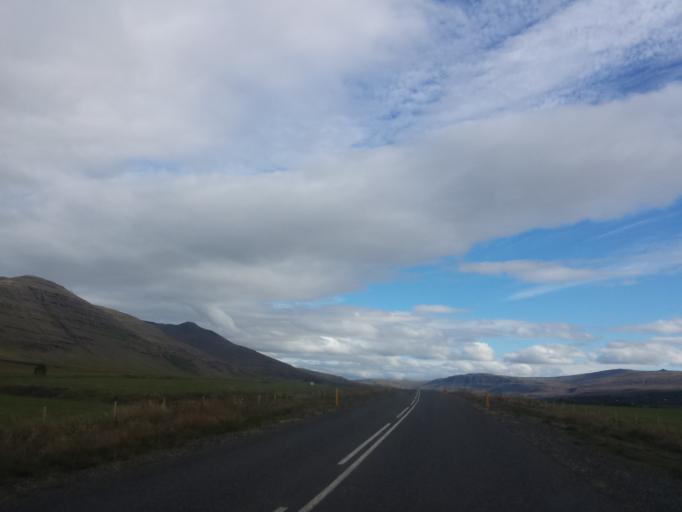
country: IS
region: West
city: Borgarnes
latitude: 64.4262
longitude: -21.7157
